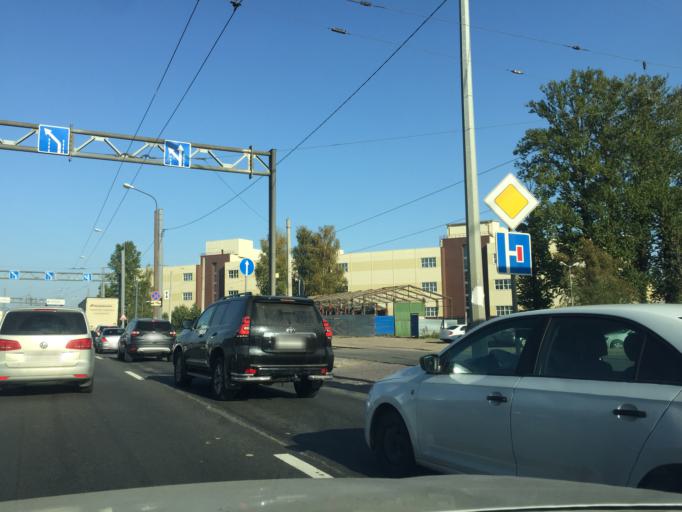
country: RU
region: St.-Petersburg
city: Krasnogvargeisky
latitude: 59.9952
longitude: 30.4372
